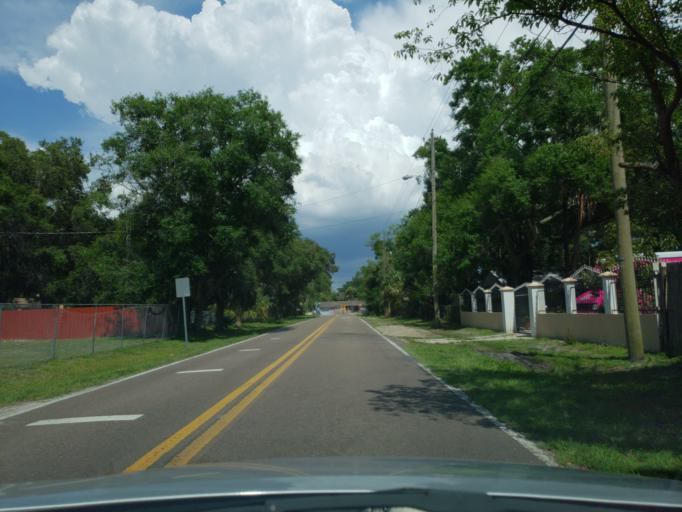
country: US
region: Florida
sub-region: Hillsborough County
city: Palm River-Clair Mel
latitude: 27.9335
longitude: -82.3778
